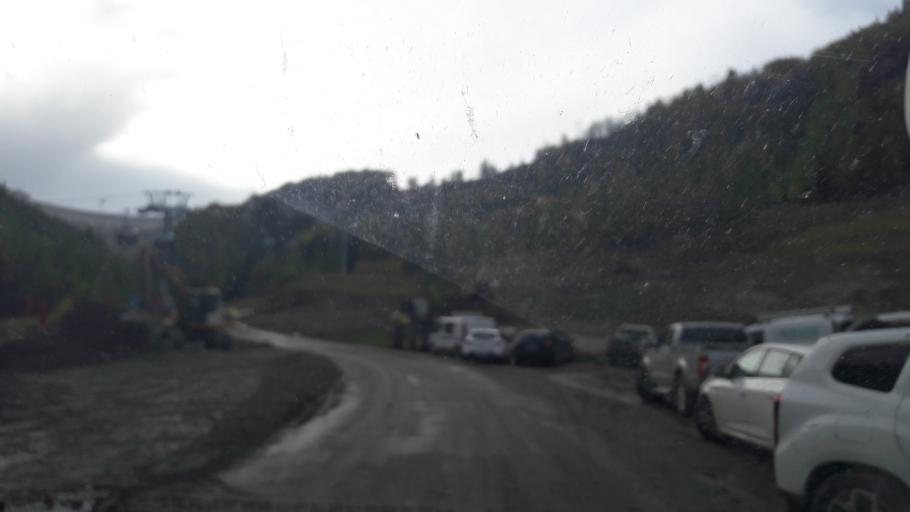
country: FR
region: Rhone-Alpes
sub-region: Departement de la Savoie
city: Tignes
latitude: 45.5067
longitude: 6.9206
